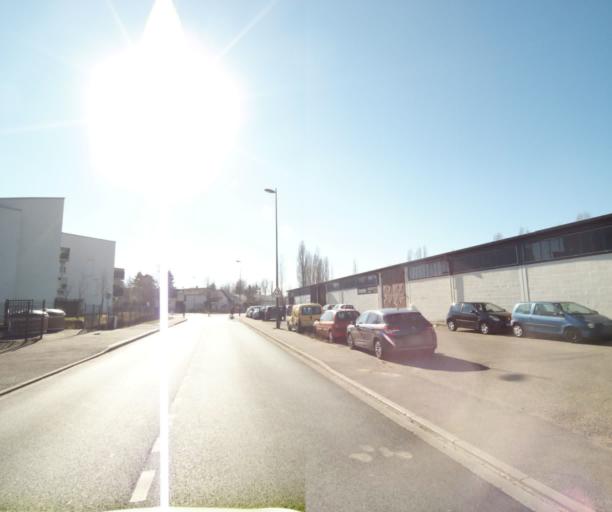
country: FR
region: Lorraine
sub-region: Departement de Meurthe-et-Moselle
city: Saulxures-les-Nancy
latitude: 48.6832
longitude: 6.2443
